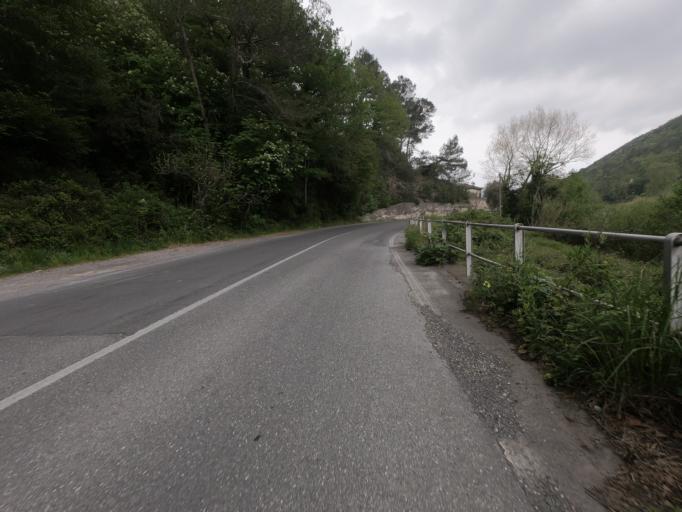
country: IT
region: Liguria
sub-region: Provincia di Savona
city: Garlenda
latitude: 44.0034
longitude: 8.0978
